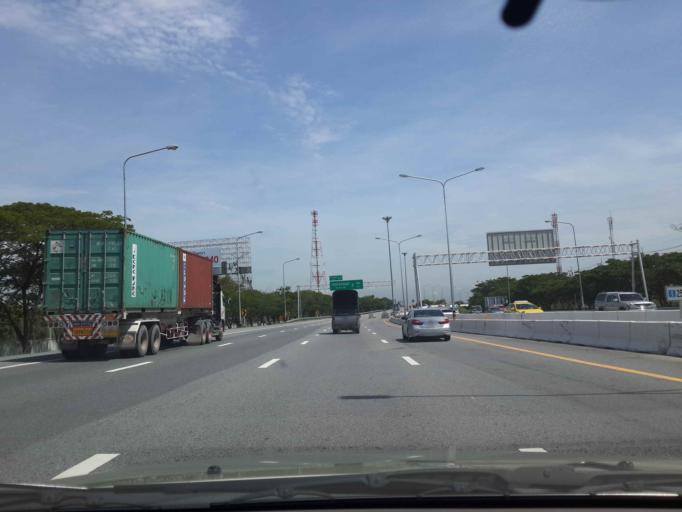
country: TH
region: Samut Prakan
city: Ban Khlong Bang Sao Thong
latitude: 13.6728
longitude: 100.8393
